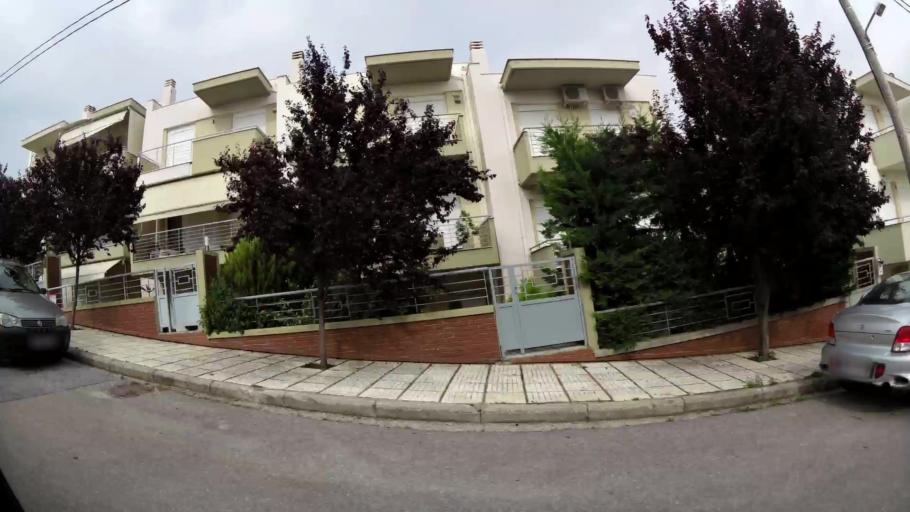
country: GR
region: Central Macedonia
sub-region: Nomos Thessalonikis
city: Oraiokastro
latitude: 40.7295
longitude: 22.9251
